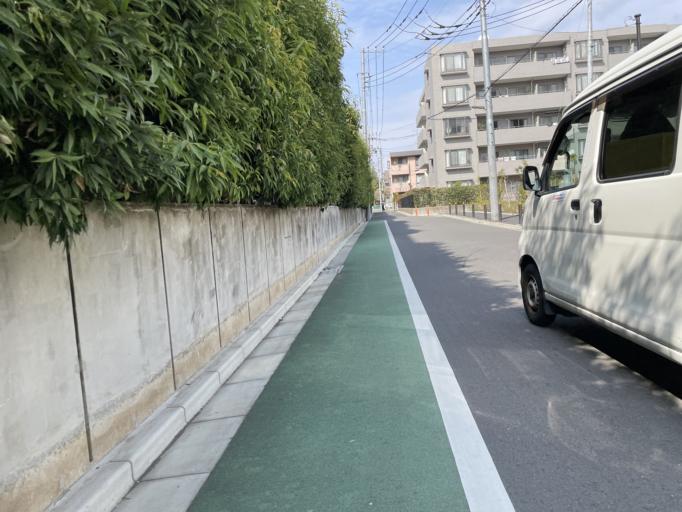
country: JP
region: Tokyo
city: Mitaka-shi
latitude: 35.6899
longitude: 139.5632
